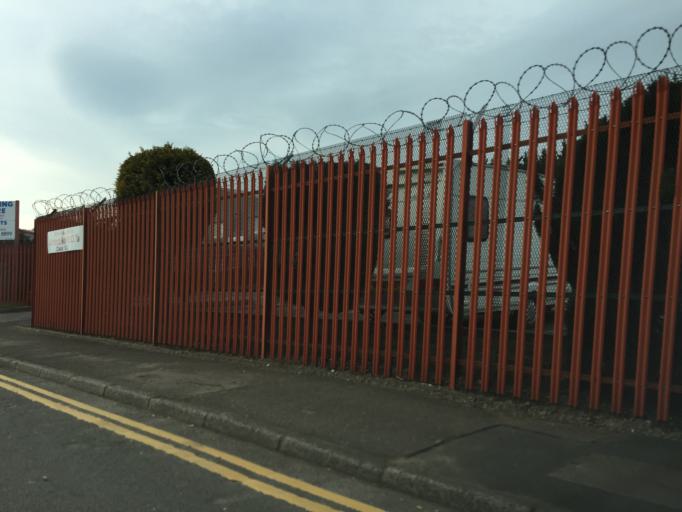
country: GB
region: Wales
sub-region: Caerphilly County Borough
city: Bedwas
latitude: 51.5934
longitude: -3.2126
